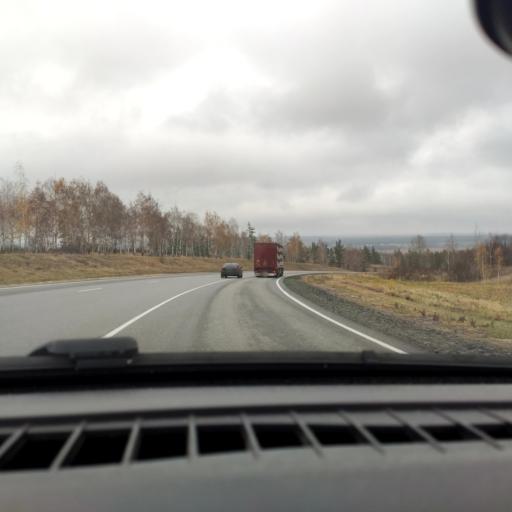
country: RU
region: Voronezj
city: Ostrogozhsk
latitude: 51.0201
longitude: 38.9813
